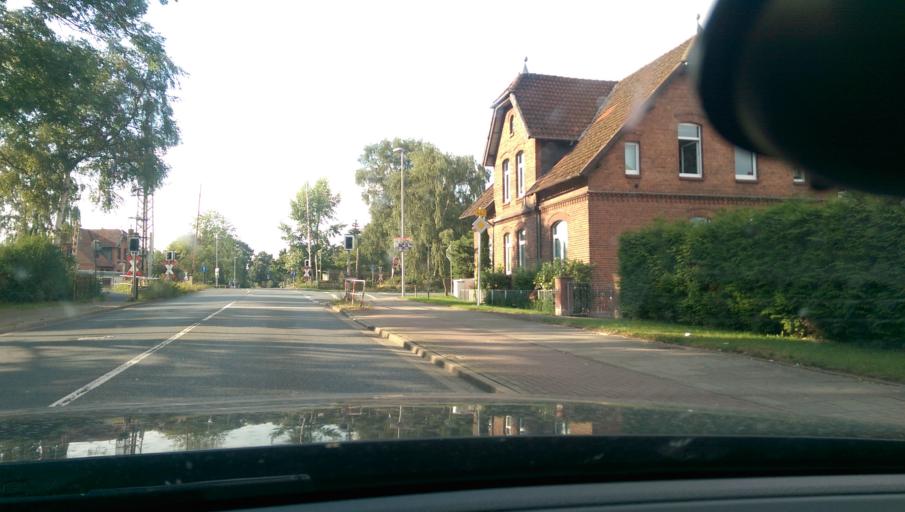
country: DE
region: Lower Saxony
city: Neustadt am Rubenberge
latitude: 52.5069
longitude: 9.4561
